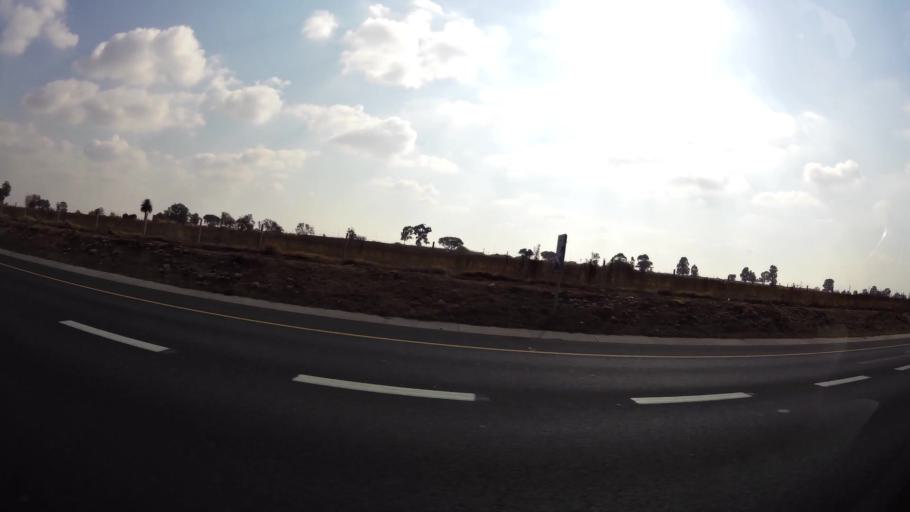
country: ZA
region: Gauteng
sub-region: Ekurhuleni Metropolitan Municipality
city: Brakpan
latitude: -26.1672
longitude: 28.3917
